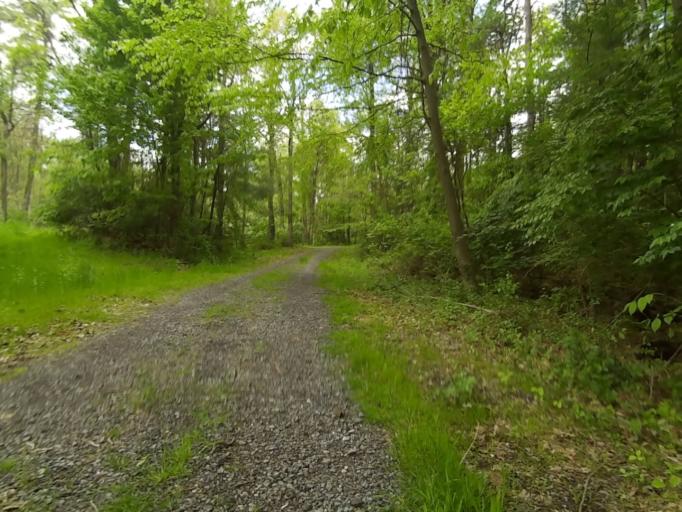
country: US
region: Pennsylvania
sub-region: Centre County
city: Park Forest Village
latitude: 40.8331
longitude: -77.9047
